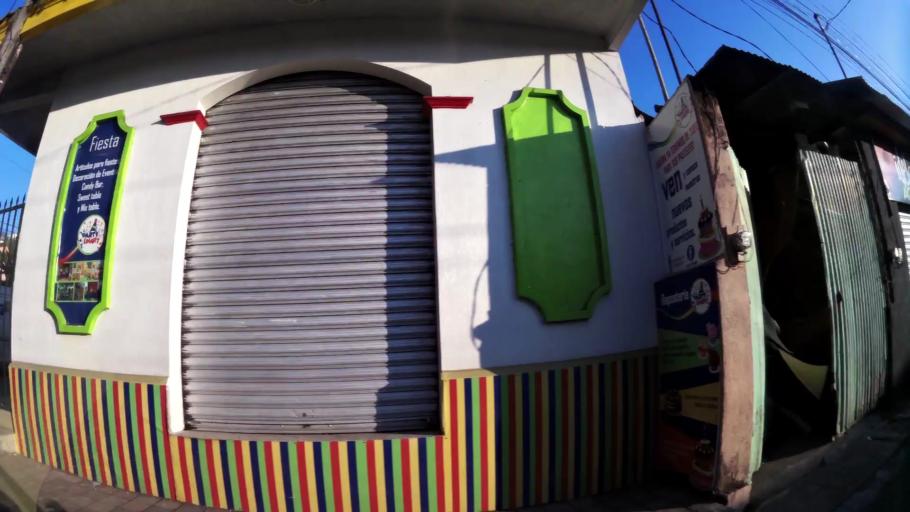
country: GT
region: Suchitepeque
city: Mazatenango
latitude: 14.5369
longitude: -91.5046
